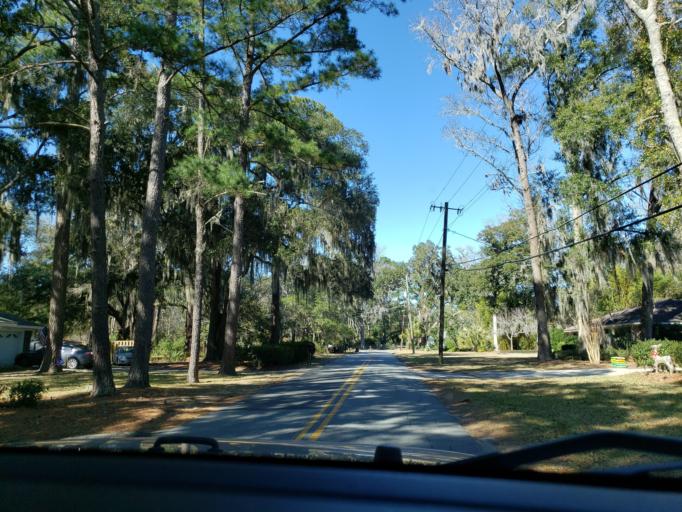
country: US
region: Georgia
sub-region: Chatham County
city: Whitemarsh Island
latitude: 32.0433
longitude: -80.9971
